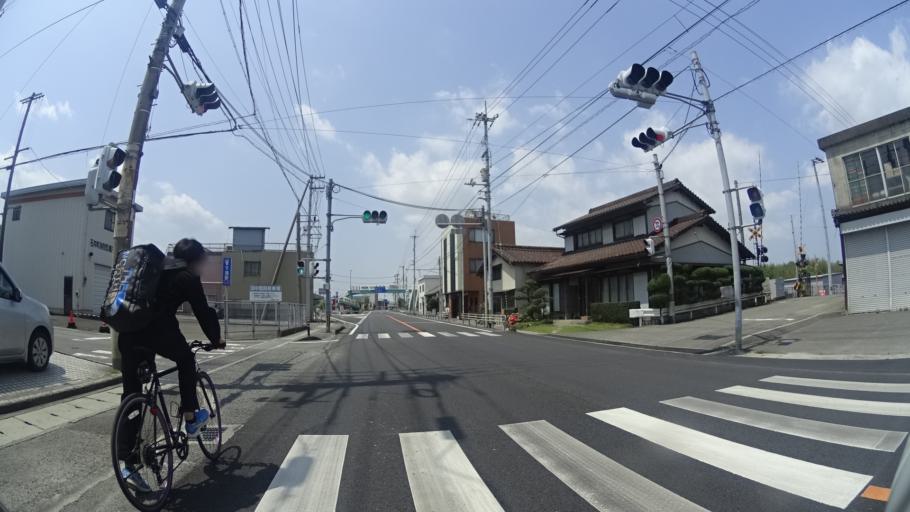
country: JP
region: Tokushima
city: Ishii
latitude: 34.0674
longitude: 134.4207
